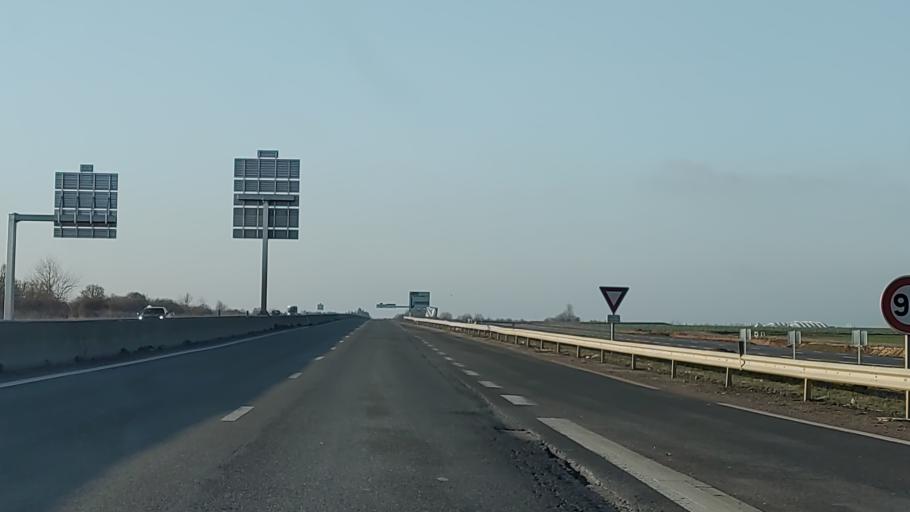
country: FR
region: Ile-de-France
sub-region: Departement de Seine-et-Marne
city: Mitry-Mory
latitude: 49.0041
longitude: 2.6274
